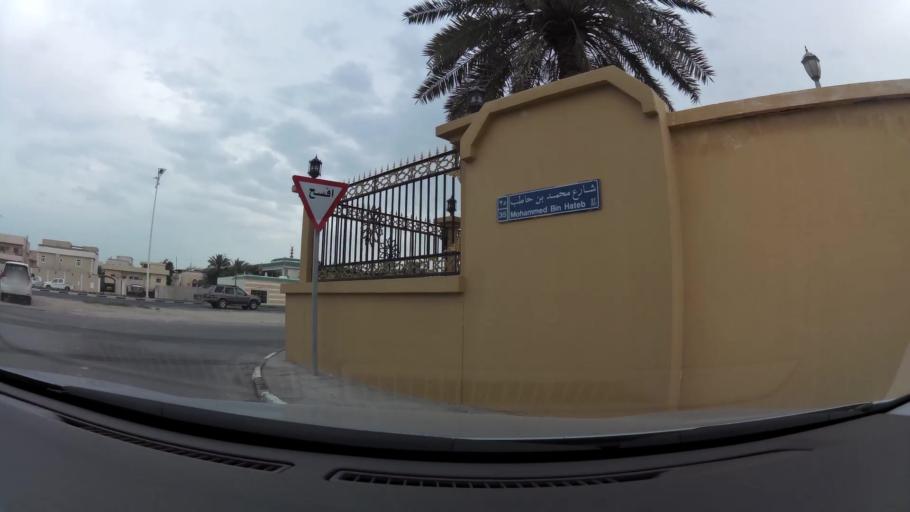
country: QA
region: Baladiyat ad Dawhah
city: Doha
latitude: 25.3098
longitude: 51.4936
